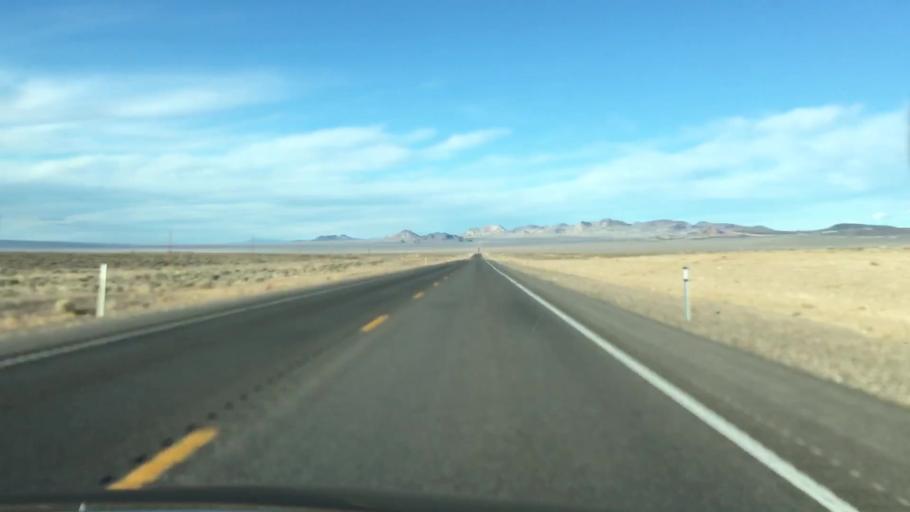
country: US
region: Nevada
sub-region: Esmeralda County
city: Goldfield
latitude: 37.8072
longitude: -117.2396
